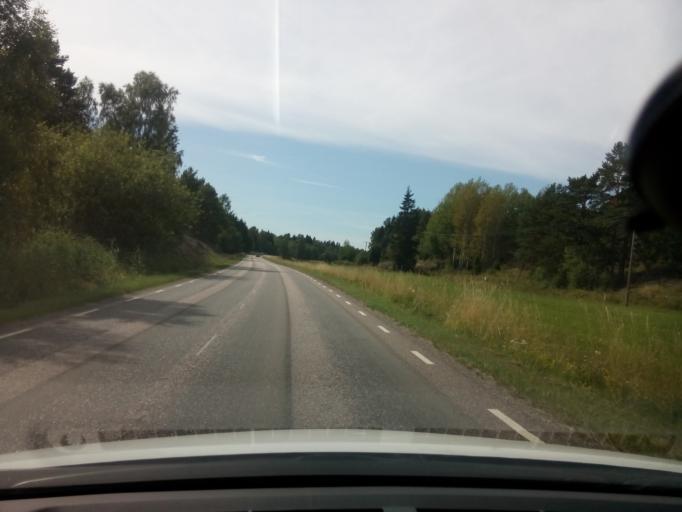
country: SE
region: Soedermanland
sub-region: Oxelosunds Kommun
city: Oxelosund
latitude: 58.7396
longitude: 17.2184
